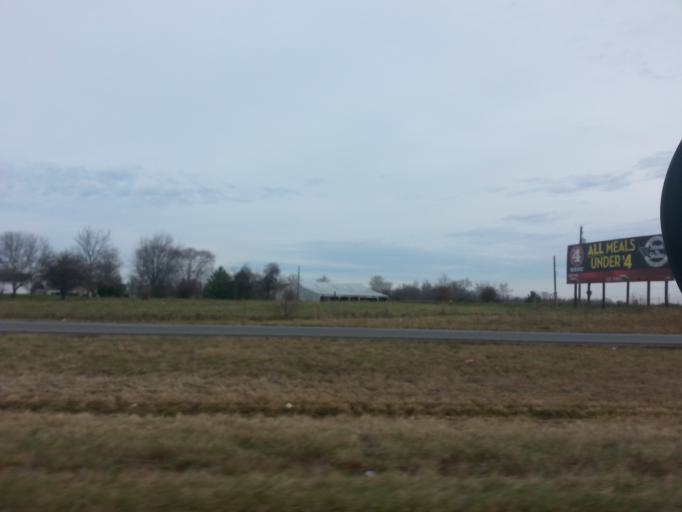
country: US
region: Indiana
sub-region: Hendricks County
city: Pittsboro
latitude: 39.8884
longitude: -86.5301
